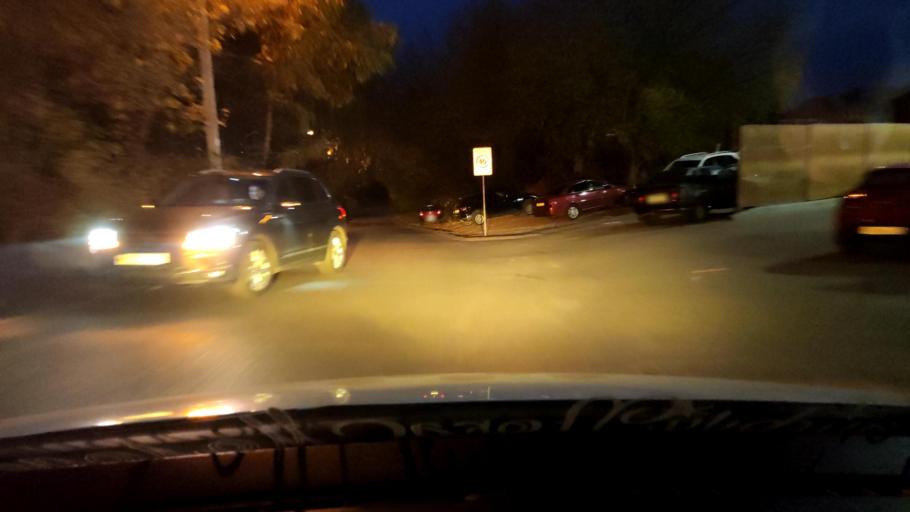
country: RU
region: Voronezj
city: Voronezh
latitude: 51.7031
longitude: 39.2049
